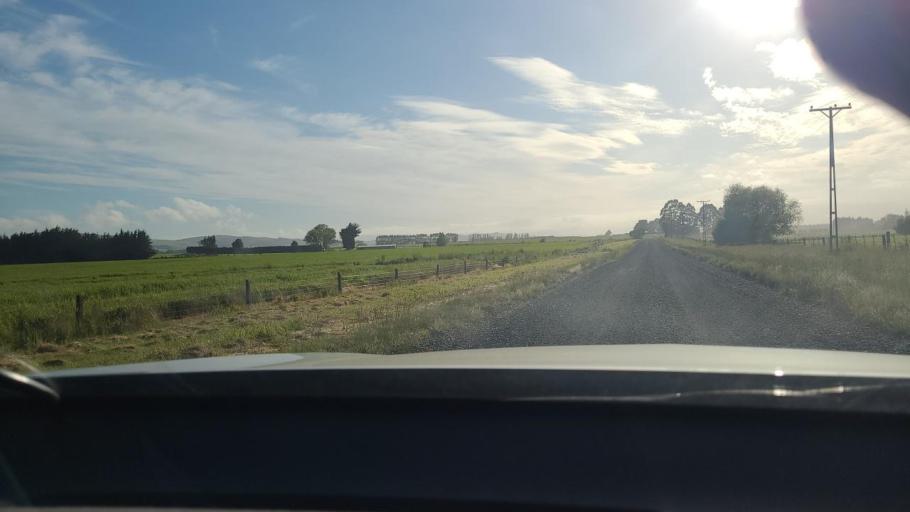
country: NZ
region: Southland
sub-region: Southland District
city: Winton
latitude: -46.0294
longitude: 168.1873
